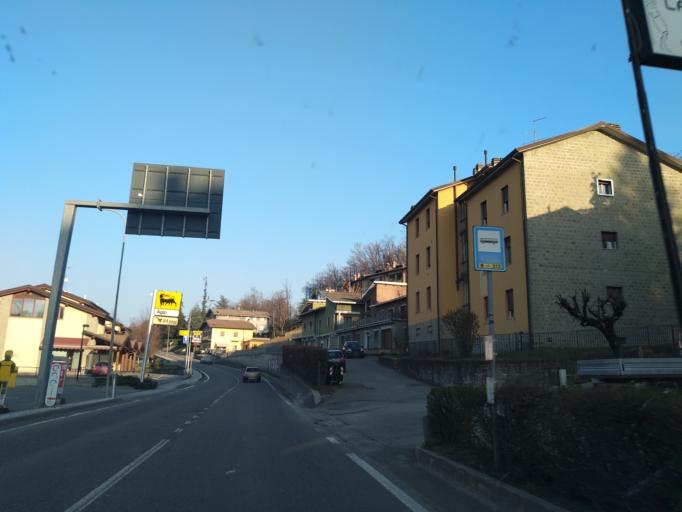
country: IT
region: Emilia-Romagna
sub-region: Provincia di Reggio Emilia
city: Castelnovo ne'Monti
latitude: 44.4321
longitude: 10.4115
